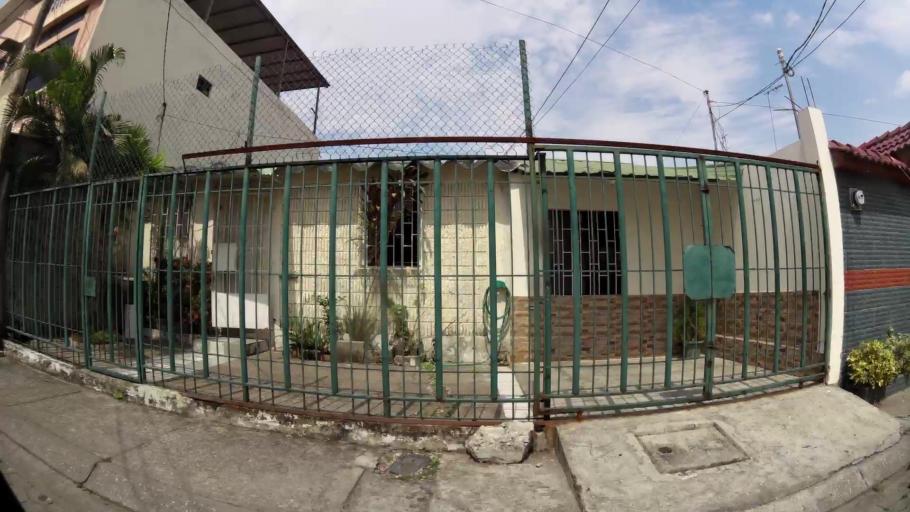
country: EC
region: Guayas
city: Eloy Alfaro
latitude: -2.1364
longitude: -79.9054
